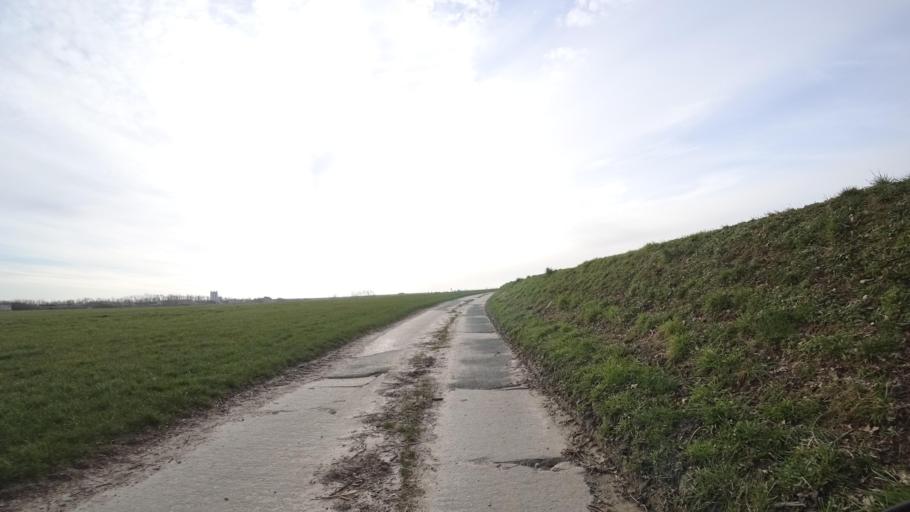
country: BE
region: Wallonia
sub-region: Province du Brabant Wallon
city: Chaumont-Gistoux
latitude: 50.6716
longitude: 4.7075
